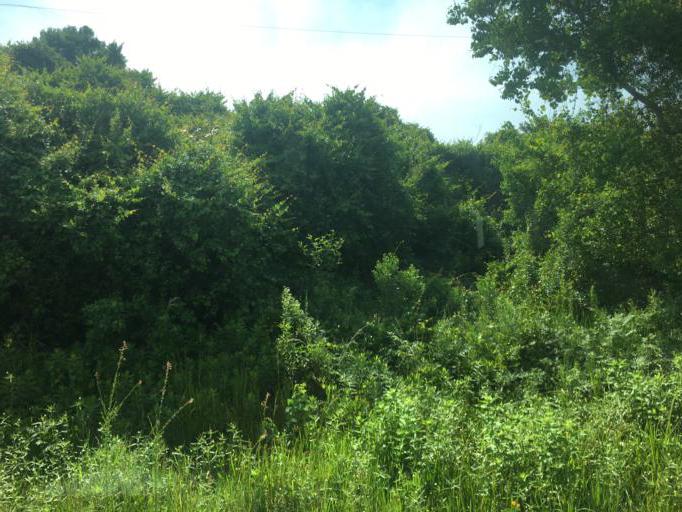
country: US
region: Florida
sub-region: Bay County
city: Laguna Beach
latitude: 30.2502
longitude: -85.9420
